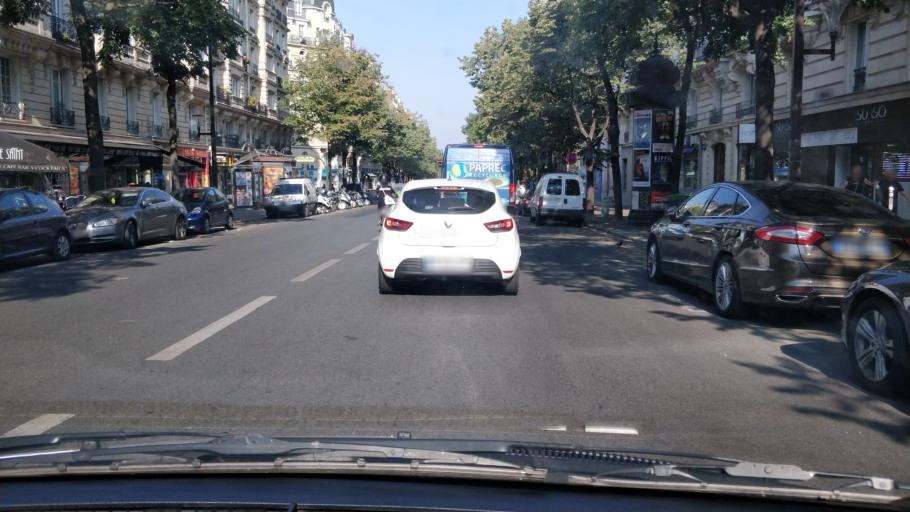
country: FR
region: Ile-de-France
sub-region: Departement de Seine-Saint-Denis
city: Le Pre-Saint-Gervais
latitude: 48.8644
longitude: 2.3794
